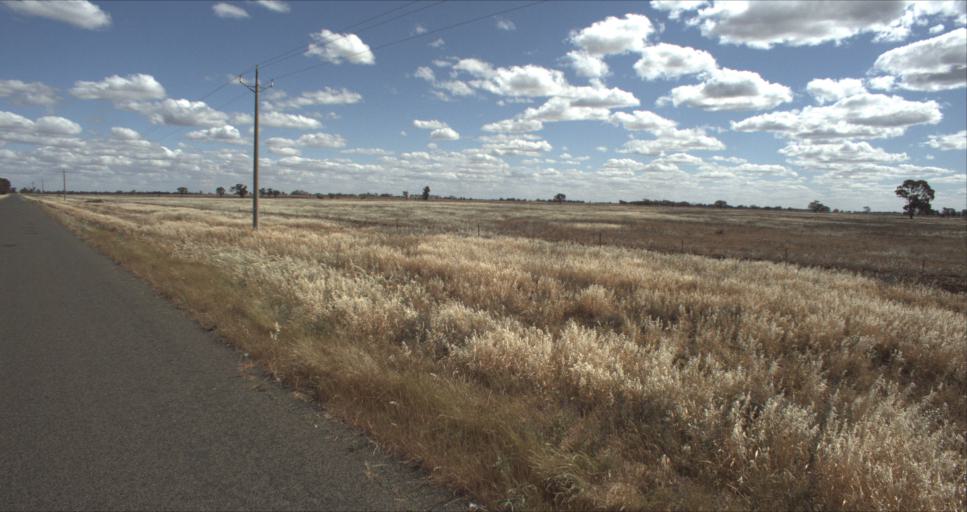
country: AU
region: New South Wales
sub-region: Leeton
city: Leeton
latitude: -34.4665
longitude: 146.2517
